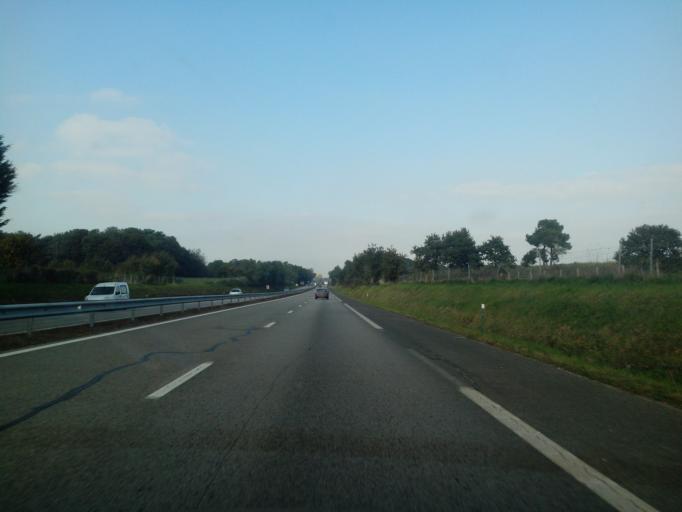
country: FR
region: Brittany
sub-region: Departement du Morbihan
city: Malestroit
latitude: 47.8409
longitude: -2.4255
